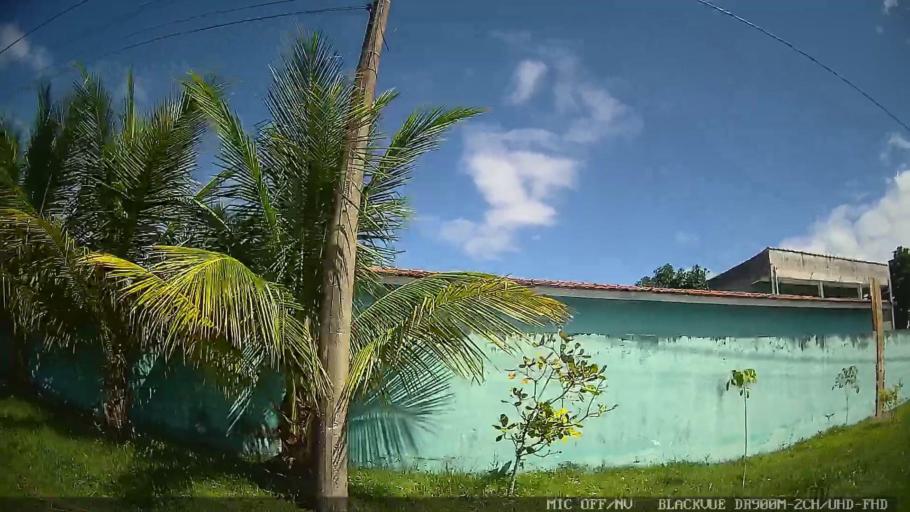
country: BR
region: Sao Paulo
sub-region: Itanhaem
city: Itanhaem
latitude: -24.2254
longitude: -46.8806
